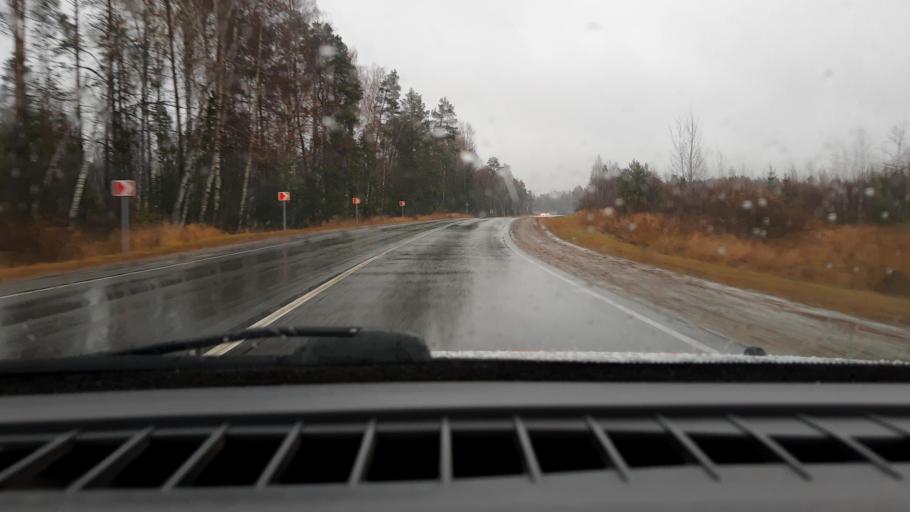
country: RU
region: Nizjnij Novgorod
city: Linda
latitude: 56.6322
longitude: 44.0937
